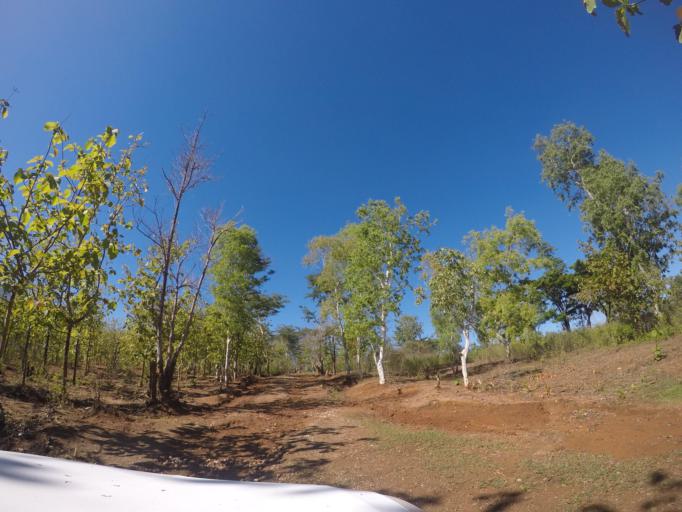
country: TL
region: Bobonaro
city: Maliana
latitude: -8.9991
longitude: 125.2044
